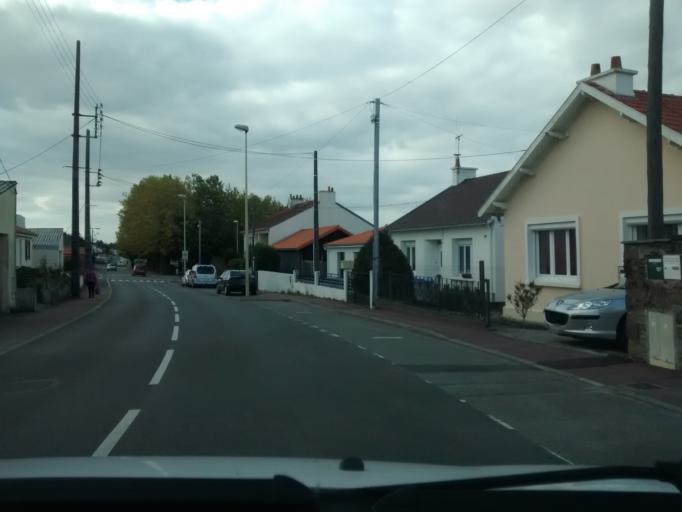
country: FR
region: Pays de la Loire
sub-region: Departement de la Loire-Atlantique
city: Le Pellerin
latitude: 47.2004
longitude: -1.7570
